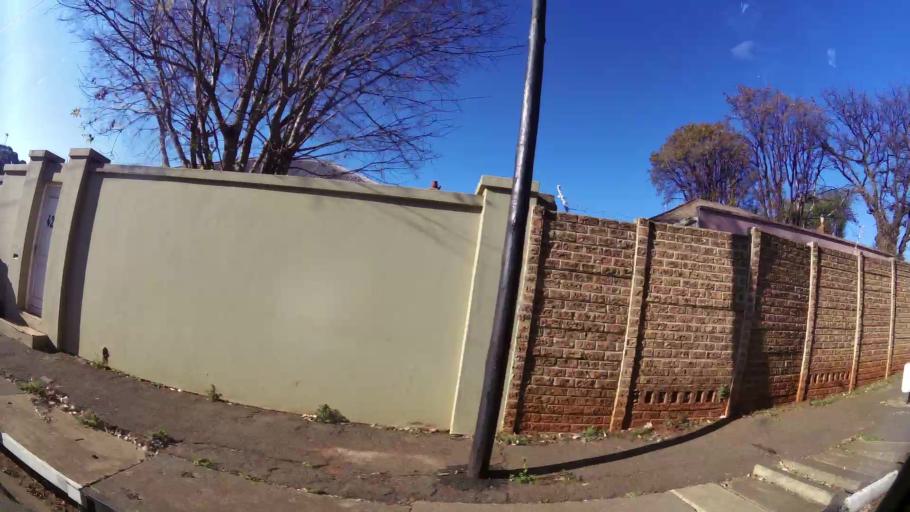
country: ZA
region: Gauteng
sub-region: City of Johannesburg Metropolitan Municipality
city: Johannesburg
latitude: -26.1912
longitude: 28.0944
